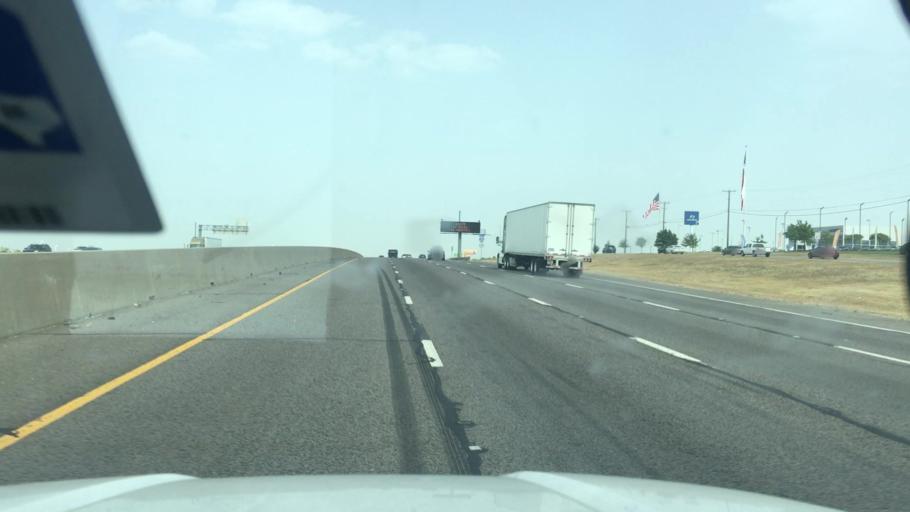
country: US
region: Texas
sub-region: Dallas County
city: DeSoto
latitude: 32.6449
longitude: -96.8523
